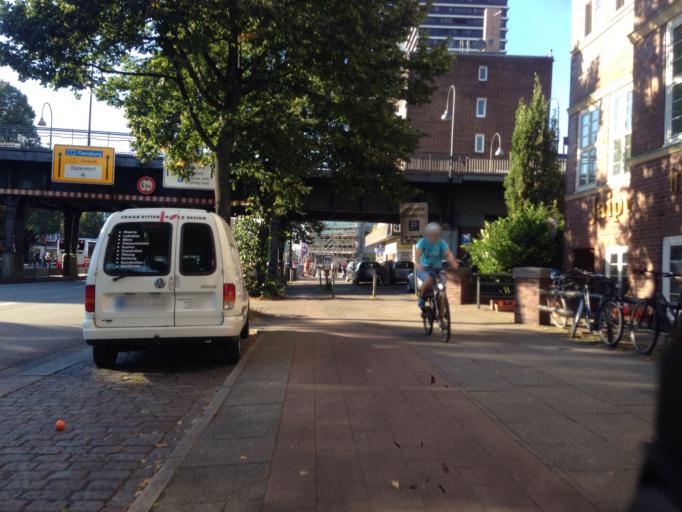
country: DE
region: Hamburg
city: Hamburg
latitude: 53.5694
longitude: 10.0285
